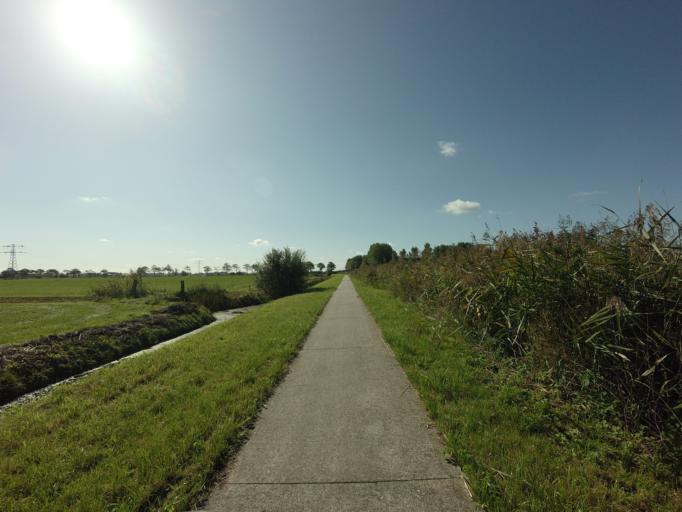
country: NL
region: Friesland
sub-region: Gemeente Leeuwarden
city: Wirdum
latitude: 53.1514
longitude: 5.7640
